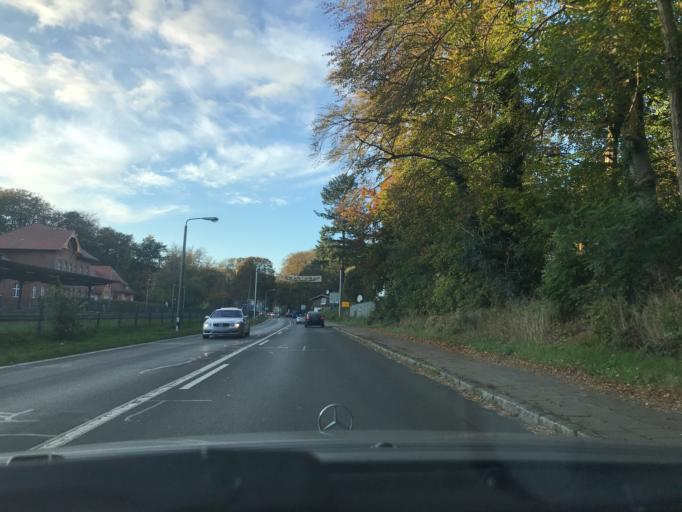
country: DE
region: Mecklenburg-Vorpommern
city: Seebad Heringsdorf
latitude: 53.9492
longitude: 14.1714
